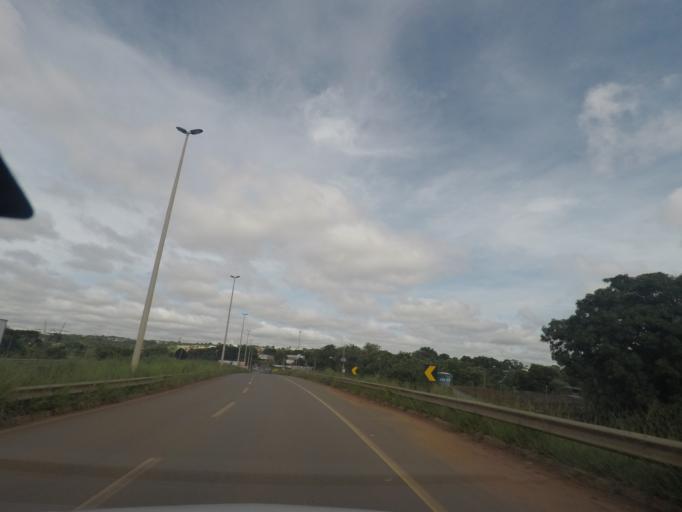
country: BR
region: Goias
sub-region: Goiania
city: Goiania
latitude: -16.6744
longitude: -49.1979
